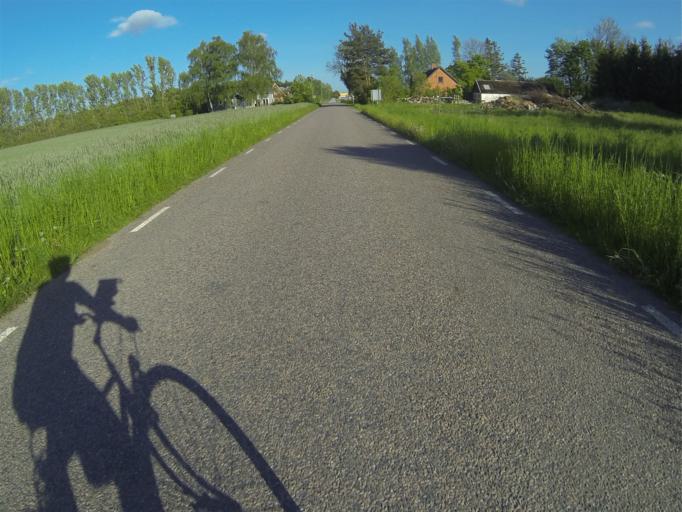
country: SE
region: Skane
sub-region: Lunds Kommun
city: Genarp
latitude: 55.7306
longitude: 13.3792
